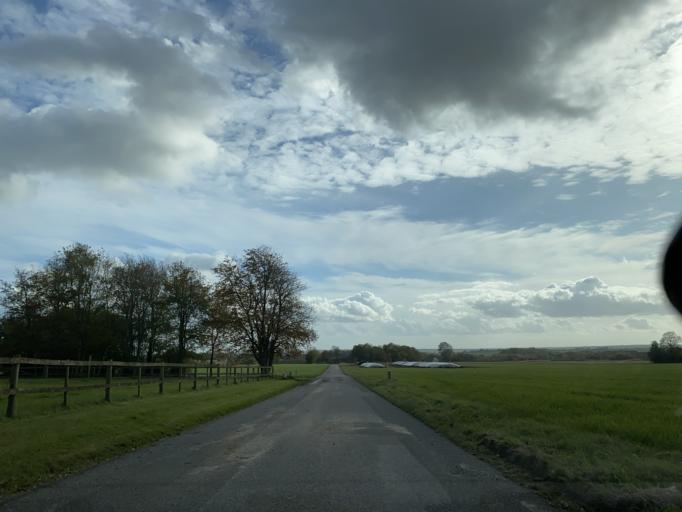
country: DK
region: Central Jutland
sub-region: Arhus Kommune
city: Sabro
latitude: 56.1971
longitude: 10.0006
